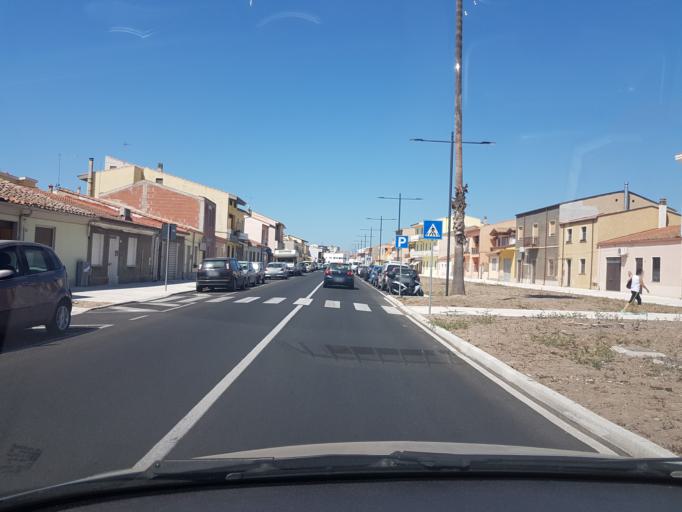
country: IT
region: Sardinia
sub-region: Provincia di Oristano
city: Oristano
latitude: 39.9000
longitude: 8.6015
